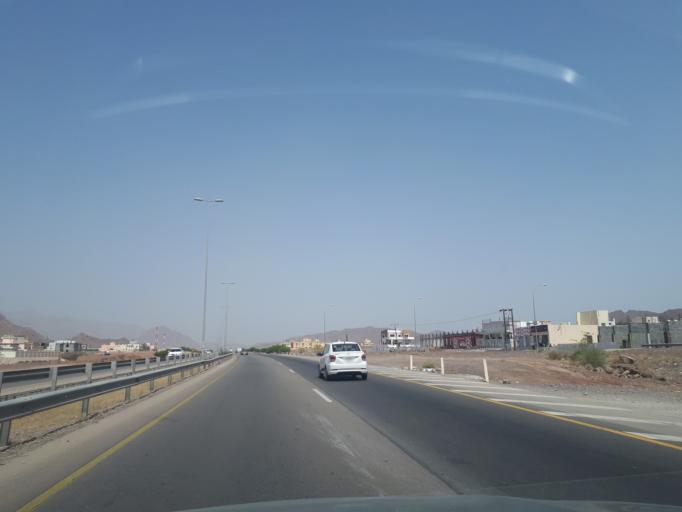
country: OM
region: Muhafazat ad Dakhiliyah
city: Bidbid
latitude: 23.4619
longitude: 58.1625
